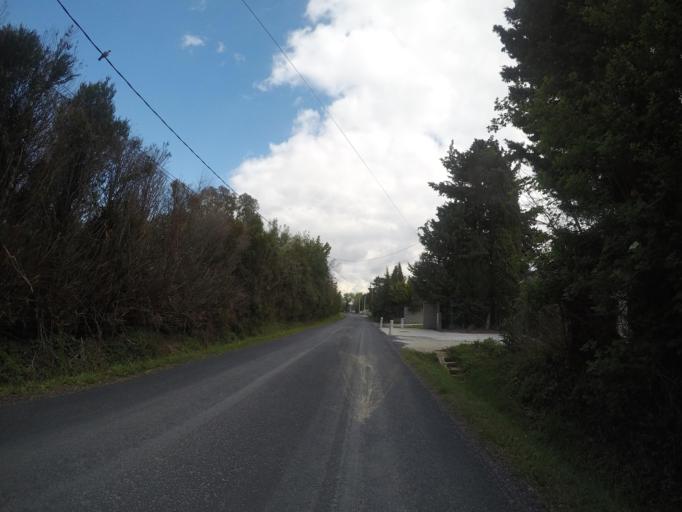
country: FR
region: Languedoc-Roussillon
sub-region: Departement des Pyrenees-Orientales
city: Le Soler
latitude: 42.6710
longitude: 2.7757
